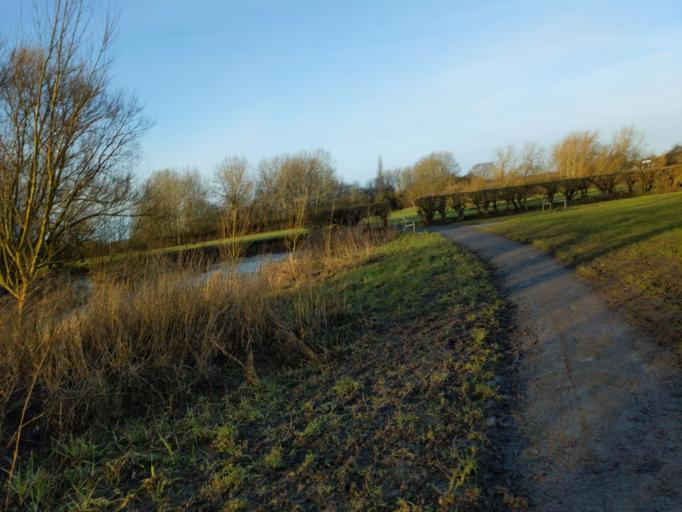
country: GB
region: England
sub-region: Essex
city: Chigwell
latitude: 51.6366
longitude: 0.0688
